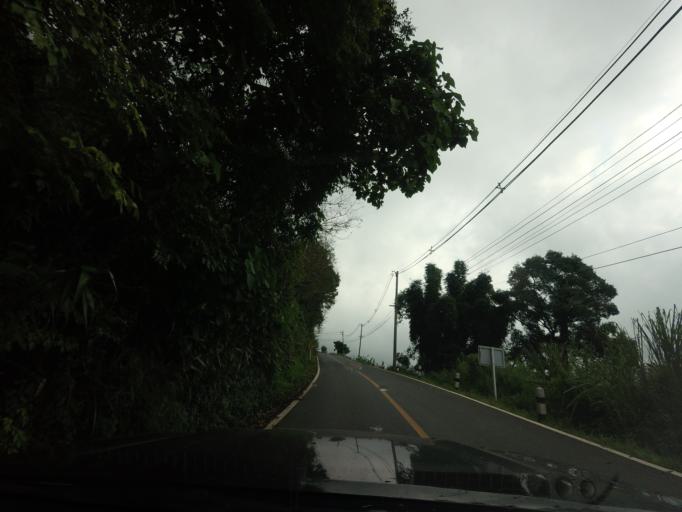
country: TH
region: Nan
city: Bo Kluea
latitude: 19.1823
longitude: 101.0760
